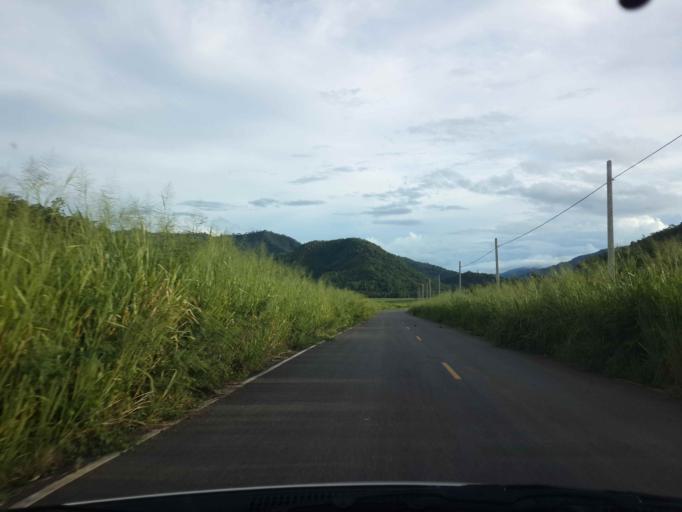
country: TH
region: Kanchanaburi
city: Dan Makham Tia
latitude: 13.7766
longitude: 99.2008
